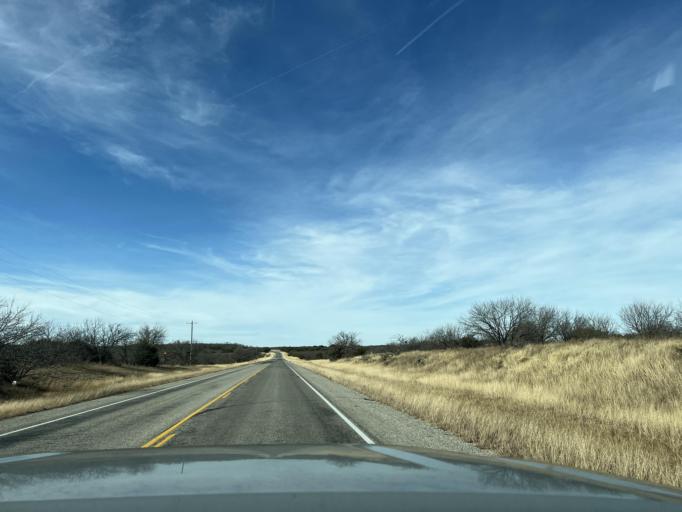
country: US
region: Texas
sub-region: Eastland County
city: Cisco
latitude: 32.4529
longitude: -98.9840
